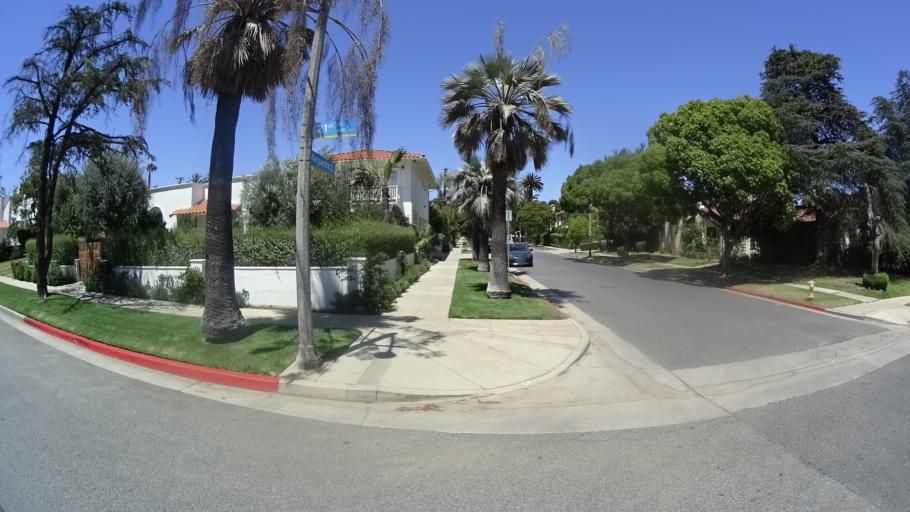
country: US
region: California
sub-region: Los Angeles County
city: Santa Monica
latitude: 34.0408
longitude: -118.4914
